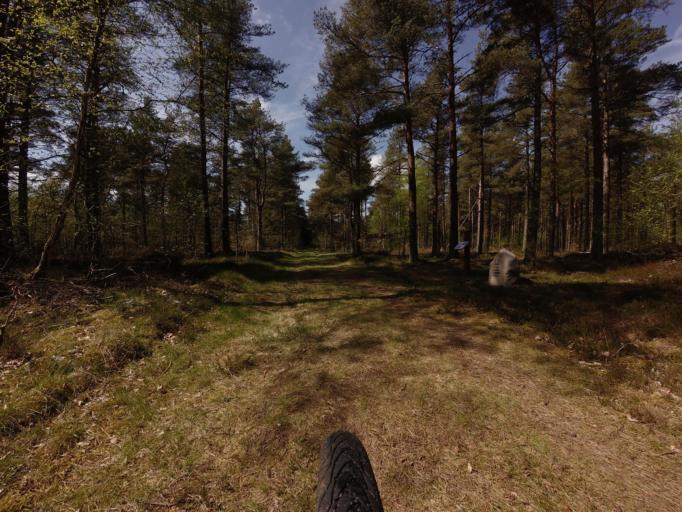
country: DK
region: North Denmark
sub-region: Jammerbugt Kommune
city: Brovst
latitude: 57.1634
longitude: 9.5732
